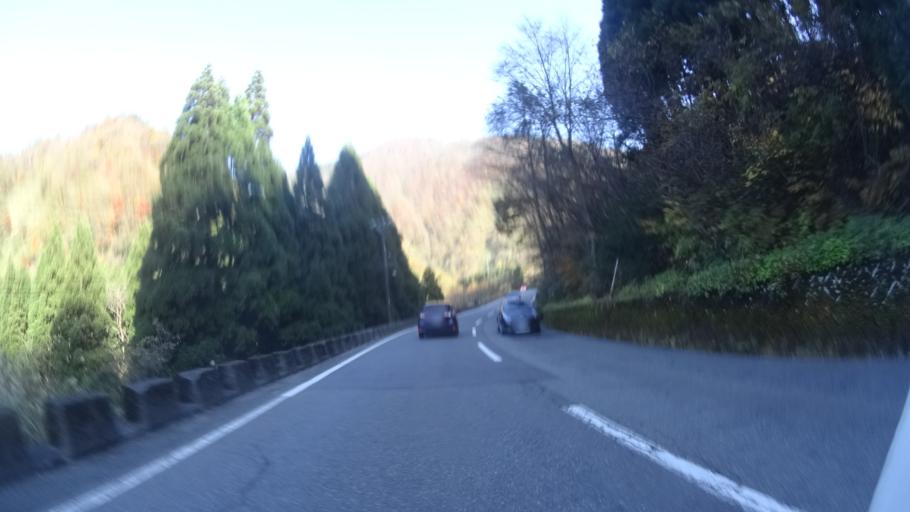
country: JP
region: Fukui
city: Ono
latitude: 35.9557
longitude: 136.6169
